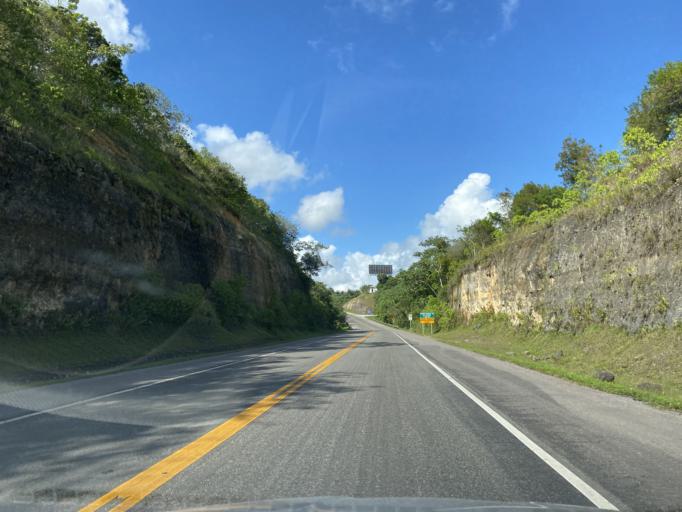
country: DO
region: Monte Plata
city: Majagual
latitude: 19.0397
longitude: -69.8285
